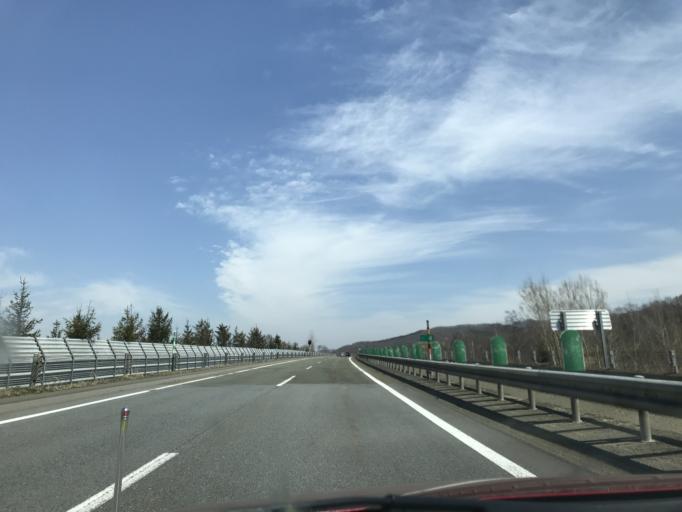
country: JP
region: Hokkaido
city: Bibai
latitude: 43.2623
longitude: 141.8379
